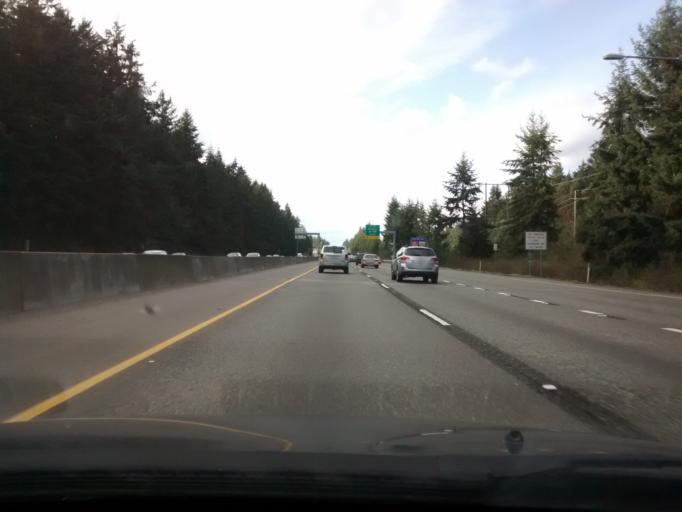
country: US
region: Washington
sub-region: Pierce County
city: Wollochet
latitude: 47.2958
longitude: -122.5680
